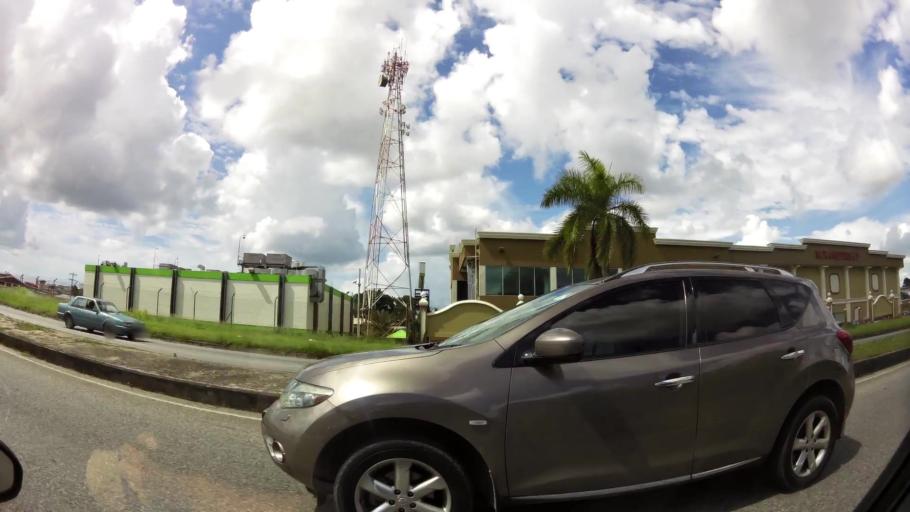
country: TT
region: City of San Fernando
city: Mon Repos
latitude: 10.2711
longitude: -61.4550
